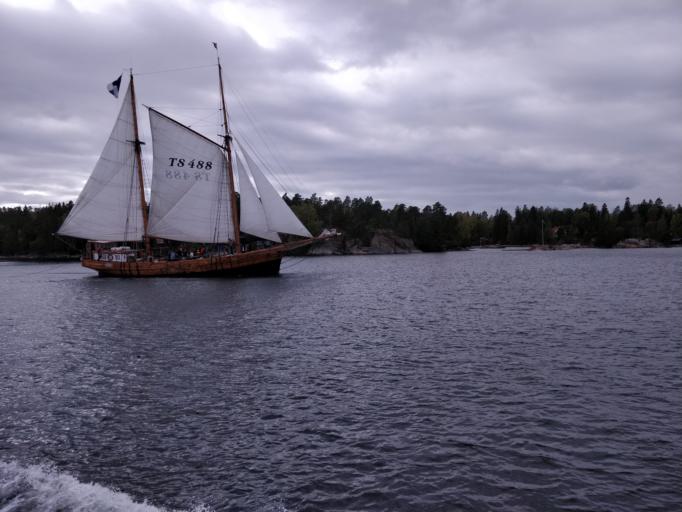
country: FI
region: Uusimaa
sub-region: Helsinki
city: Vantaa
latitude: 60.1702
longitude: 25.0950
